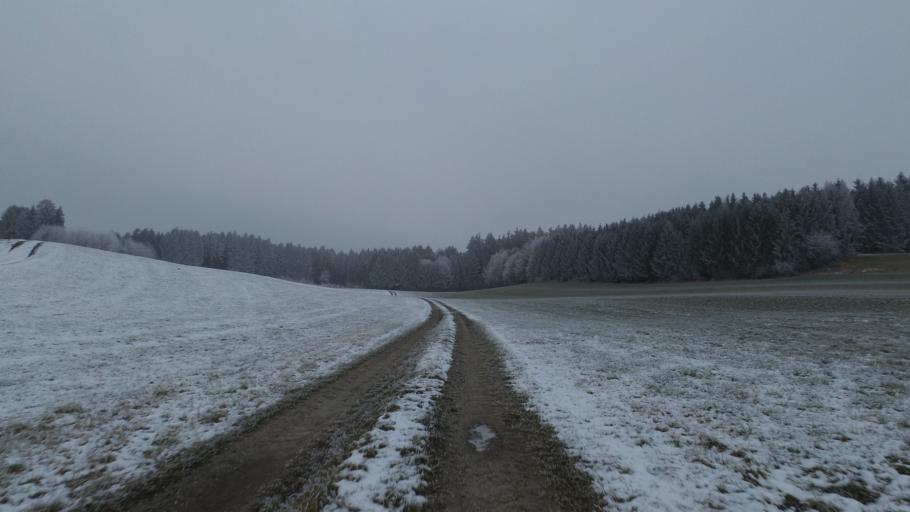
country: DE
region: Bavaria
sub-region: Upper Bavaria
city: Nussdorf
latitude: 47.8911
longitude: 12.5875
